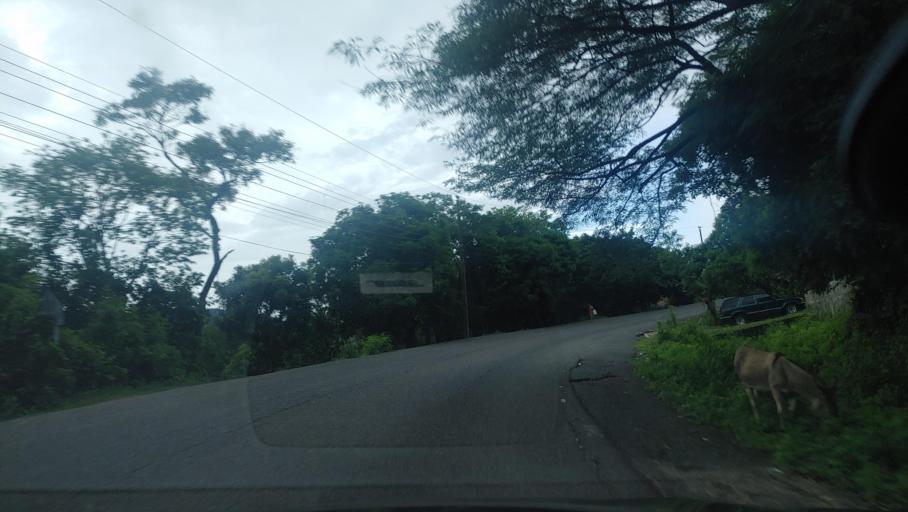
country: HN
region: Choluteca
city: Corpus
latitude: 13.3714
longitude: -86.9975
